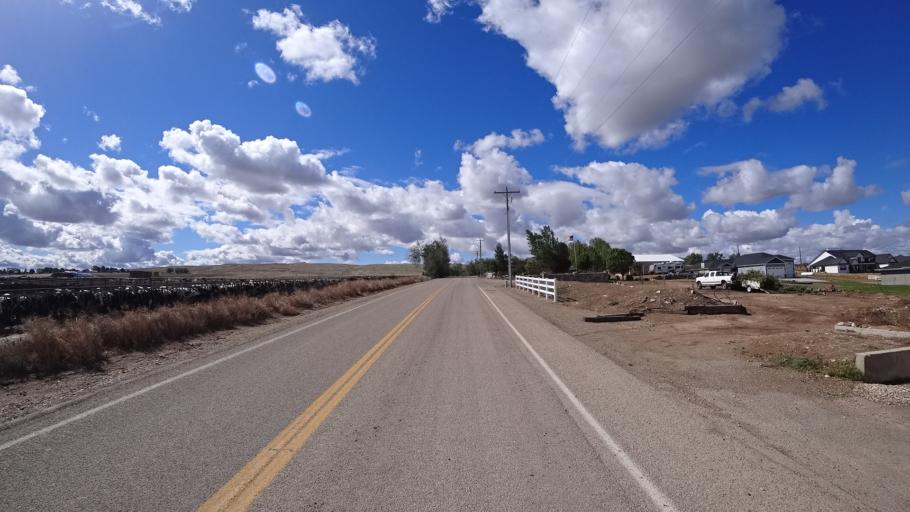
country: US
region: Idaho
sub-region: Ada County
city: Kuna
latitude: 43.4661
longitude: -116.4636
